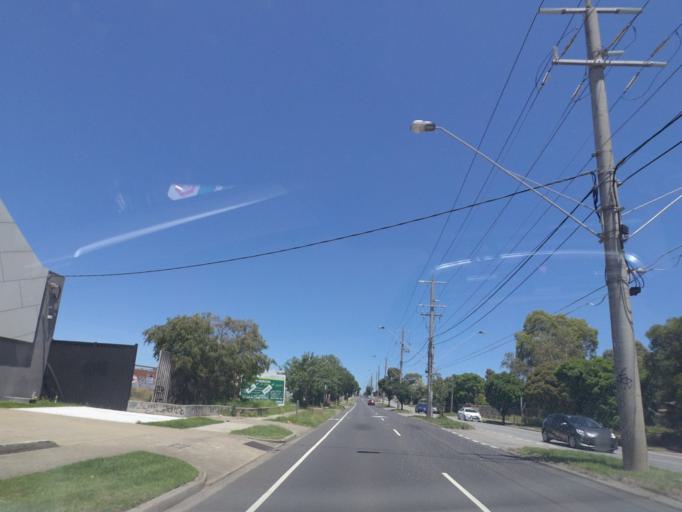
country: AU
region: Victoria
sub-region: Darebin
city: Preston
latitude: -37.7491
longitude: 145.0216
